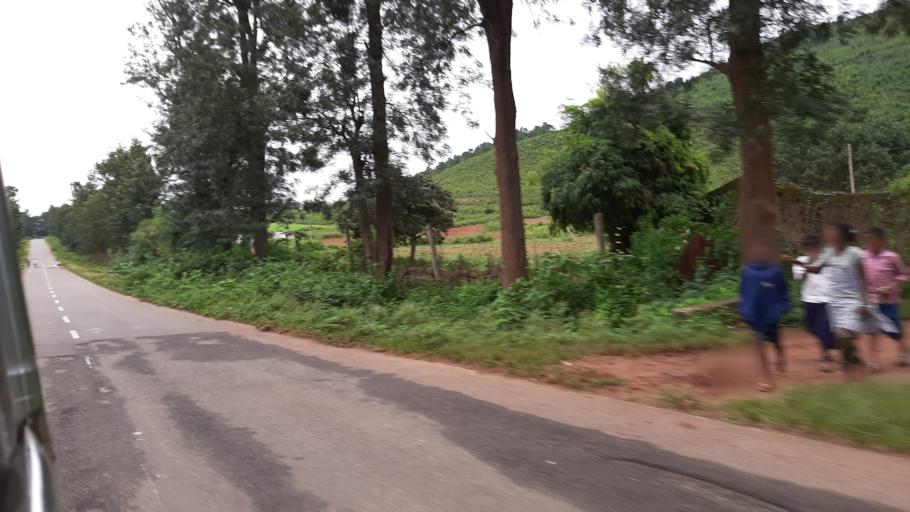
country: IN
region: Andhra Pradesh
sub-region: Vizianagaram District
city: Salur
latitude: 18.2935
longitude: 82.9181
